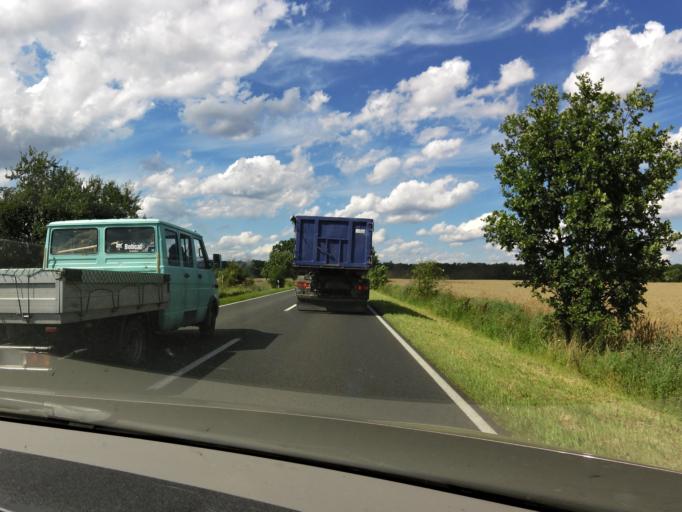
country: DE
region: Brandenburg
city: Gransee
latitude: 53.0514
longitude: 13.1935
